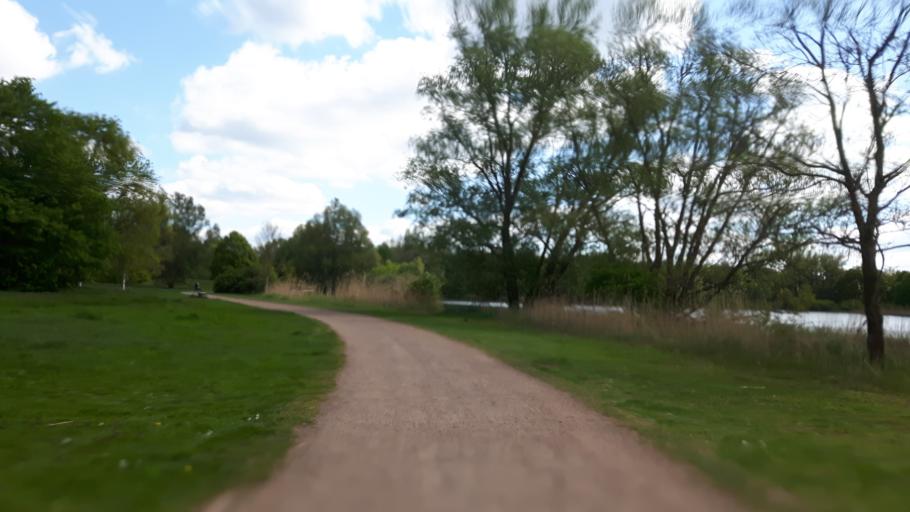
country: DE
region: Bremen
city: Bremen
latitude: 53.0445
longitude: 8.8390
